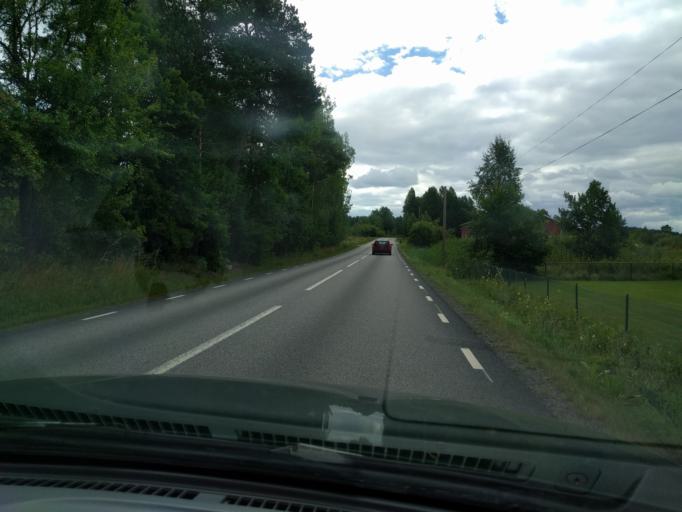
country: SE
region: Soedermanland
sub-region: Nykopings Kommun
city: Svalsta
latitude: 58.5336
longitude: 16.7445
